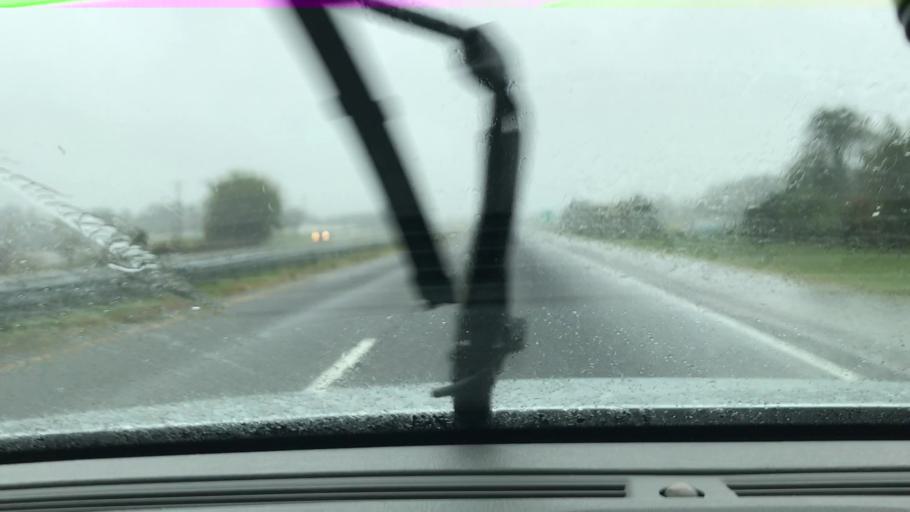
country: US
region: Alabama
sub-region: Limestone County
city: Ardmore
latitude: 34.9658
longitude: -86.8865
